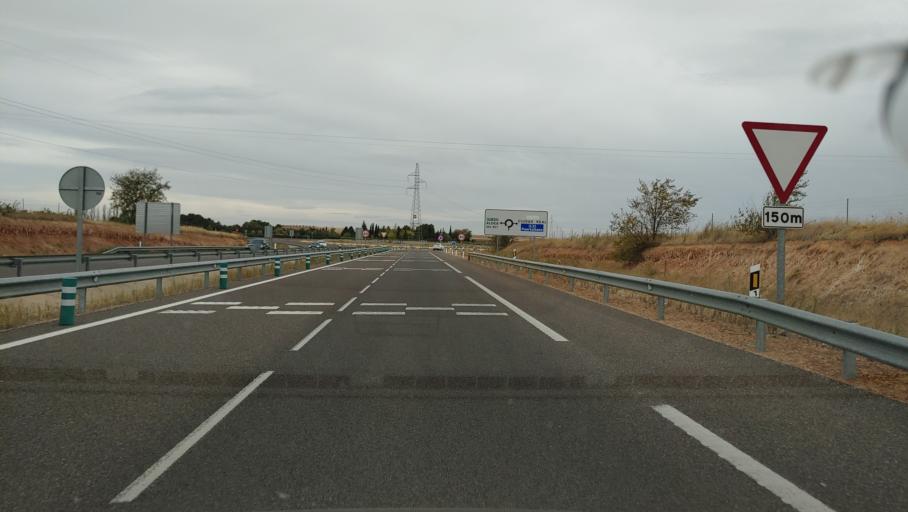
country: ES
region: Castille-La Mancha
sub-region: Provincia de Ciudad Real
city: Miguelturra
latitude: 38.9471
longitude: -3.9137
